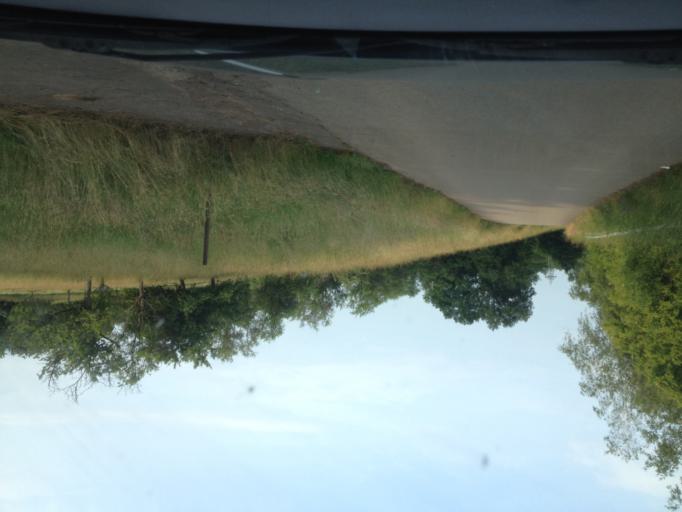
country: DE
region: Saarland
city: Mainzweiler
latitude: 49.4364
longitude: 7.1476
